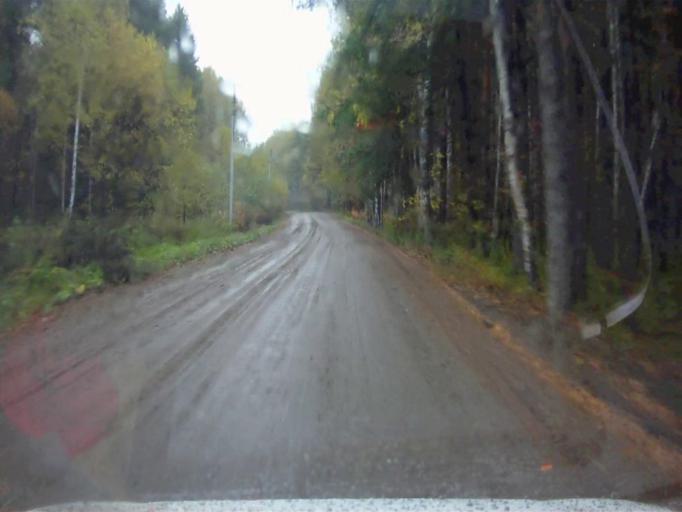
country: RU
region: Chelyabinsk
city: Kyshtym
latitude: 55.8955
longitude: 60.4652
